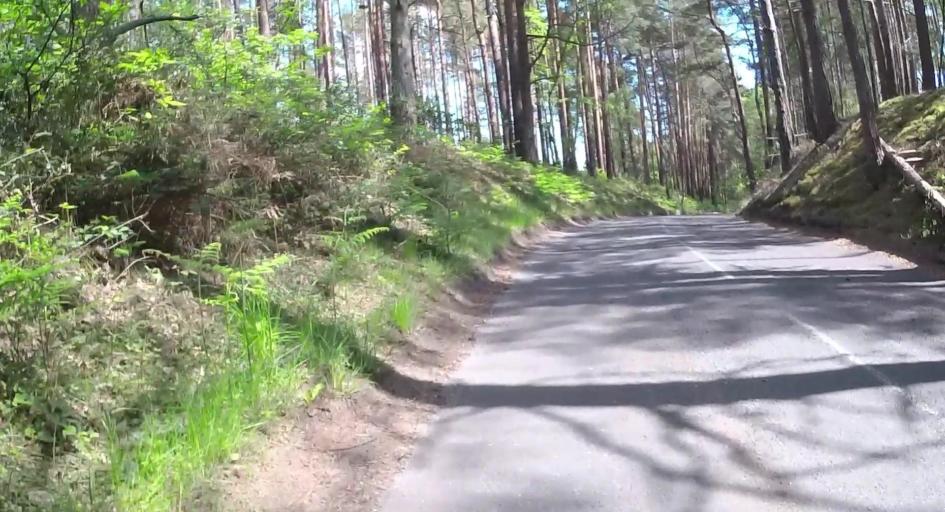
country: GB
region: England
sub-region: Surrey
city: Farnham
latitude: 51.1857
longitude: -0.7823
